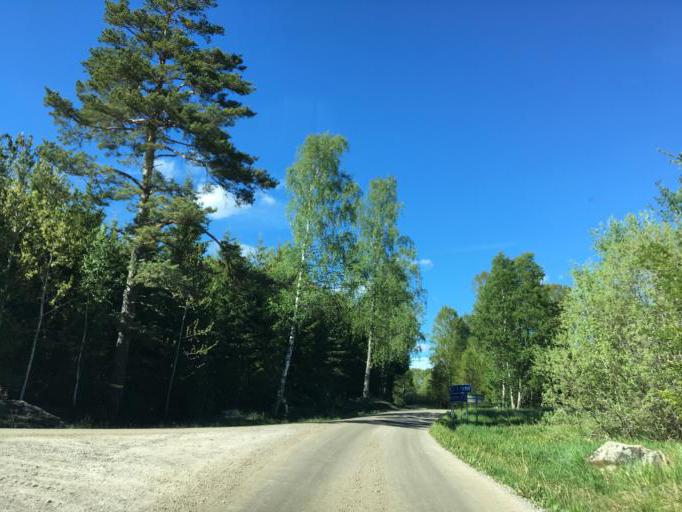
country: SE
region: Soedermanland
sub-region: Eskilstuna Kommun
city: Kvicksund
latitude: 59.3927
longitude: 16.2361
